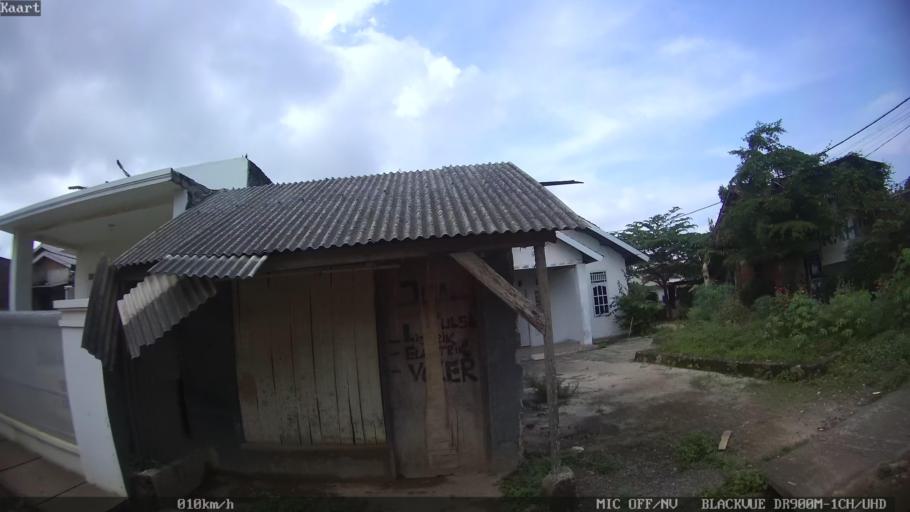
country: ID
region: Lampung
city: Kedaton
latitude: -5.3316
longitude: 105.2903
